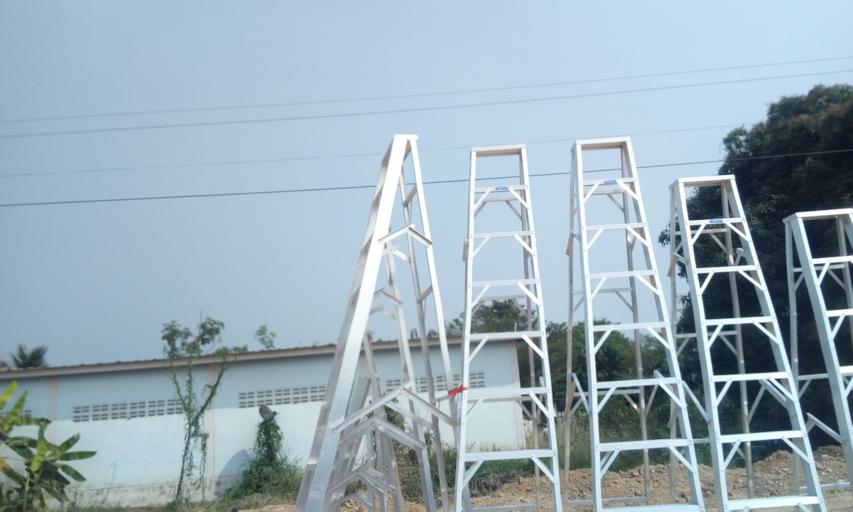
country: TH
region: Pathum Thani
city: Lam Luk Ka
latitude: 13.9646
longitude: 100.7257
